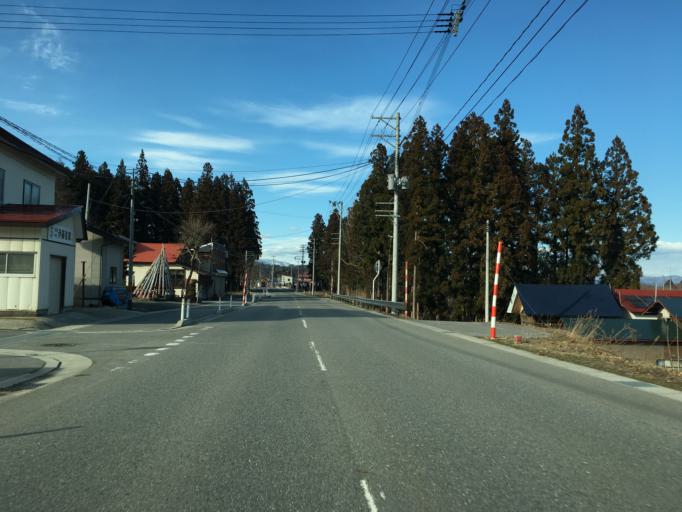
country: JP
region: Yamagata
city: Nagai
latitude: 38.0032
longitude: 139.9599
